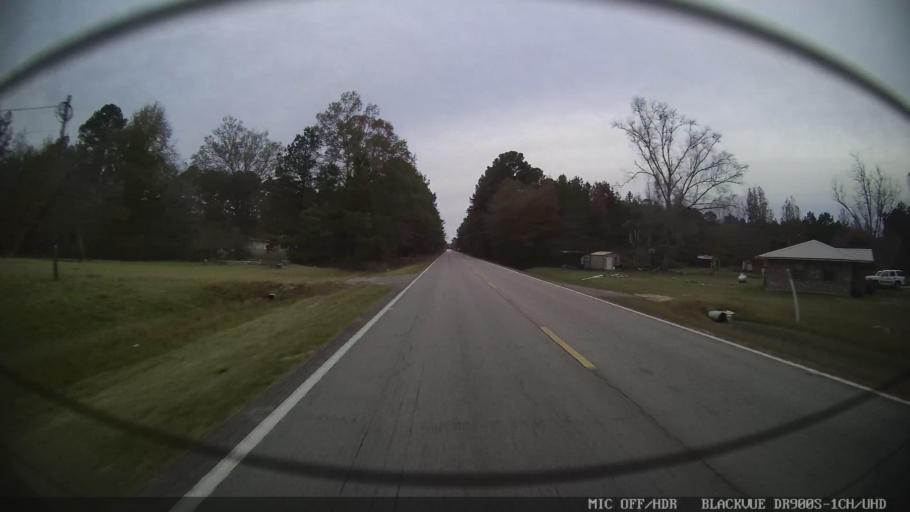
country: US
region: Mississippi
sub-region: Clarke County
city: Stonewall
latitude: 32.0301
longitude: -88.8659
